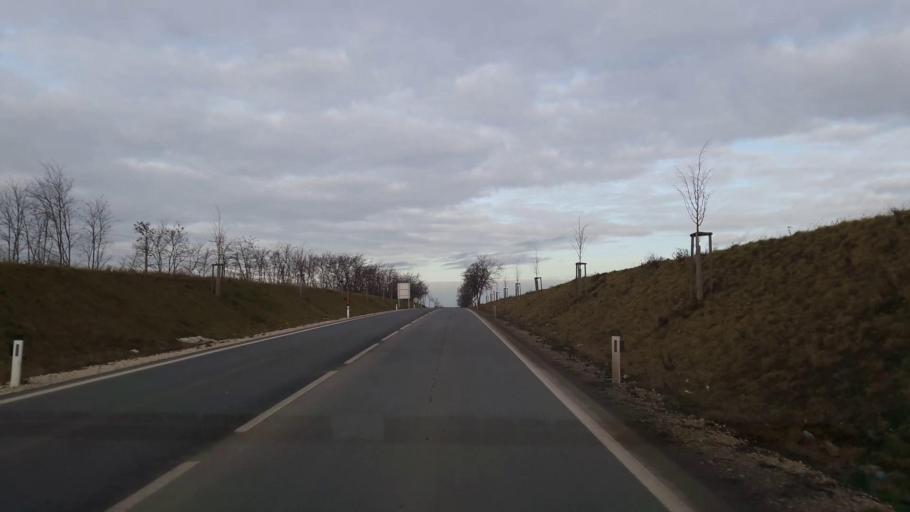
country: AT
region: Lower Austria
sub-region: Politischer Bezirk Mistelbach
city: Mistelbach
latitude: 48.5855
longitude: 16.5570
